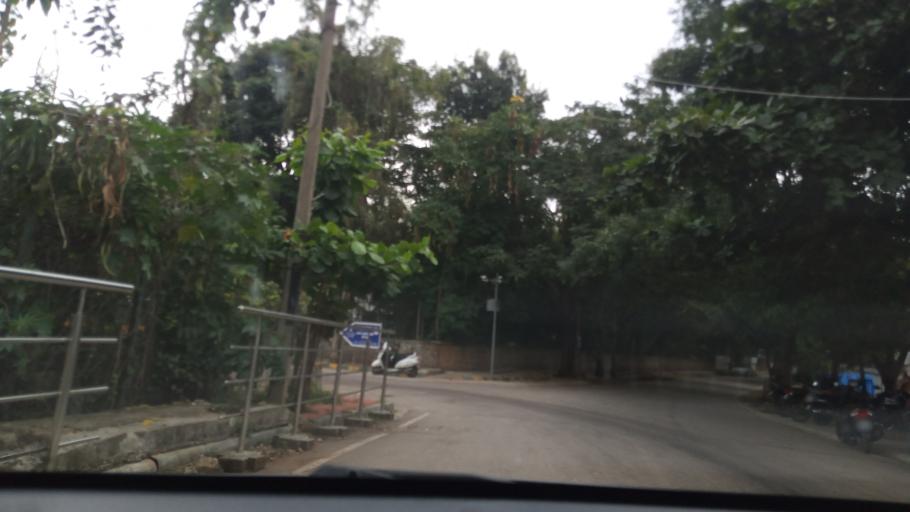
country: IN
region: Karnataka
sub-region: Bangalore Urban
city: Bangalore
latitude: 13.0118
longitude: 77.5379
